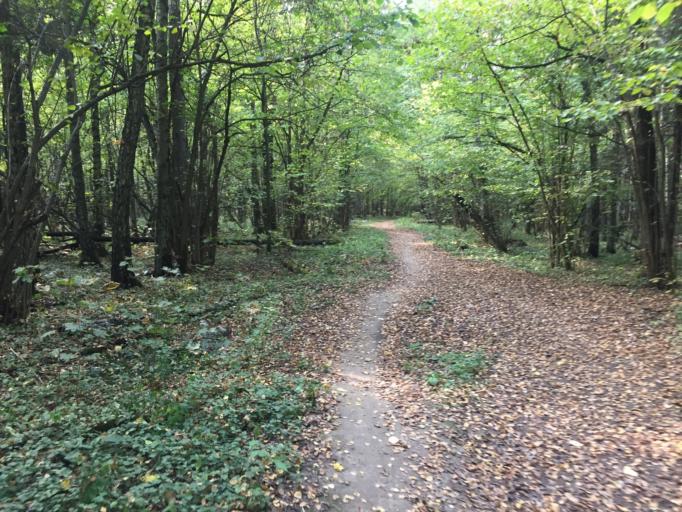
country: RU
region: Moscow
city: Babushkin
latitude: 55.8677
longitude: 37.7422
